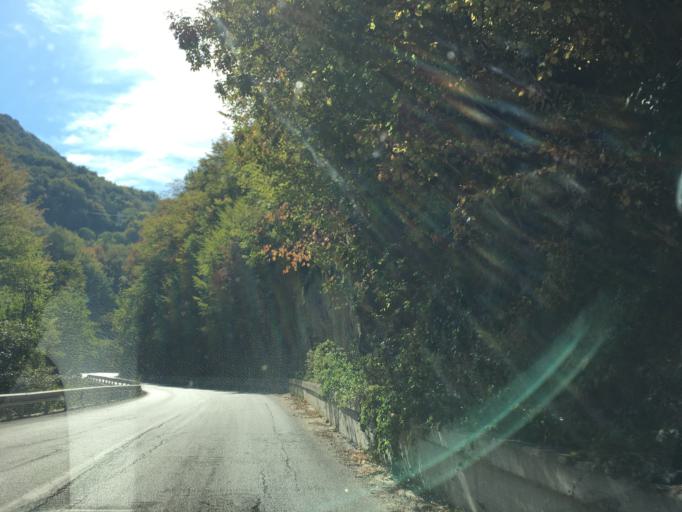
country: BG
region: Pazardzhik
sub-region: Obshtina Peshtera
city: Peshtera
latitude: 42.0017
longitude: 24.2539
